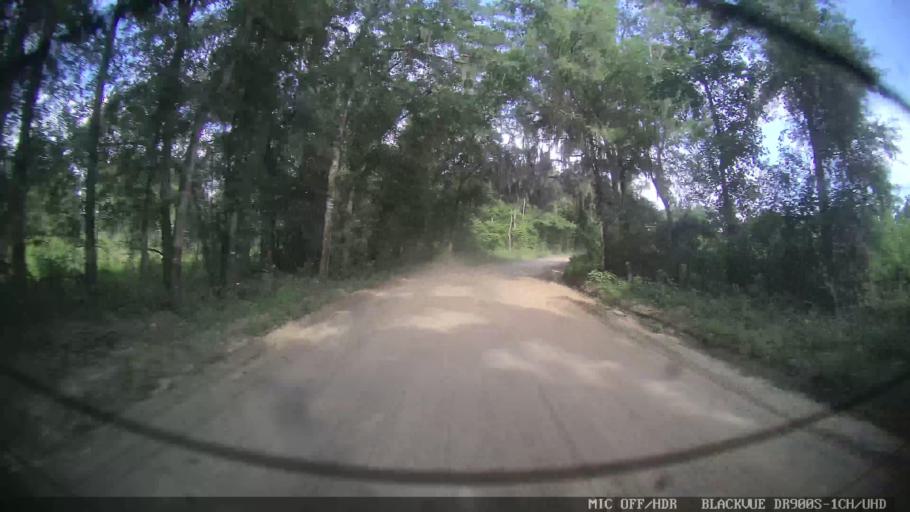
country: US
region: Georgia
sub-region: Lowndes County
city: Valdosta
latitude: 30.6204
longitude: -83.2416
